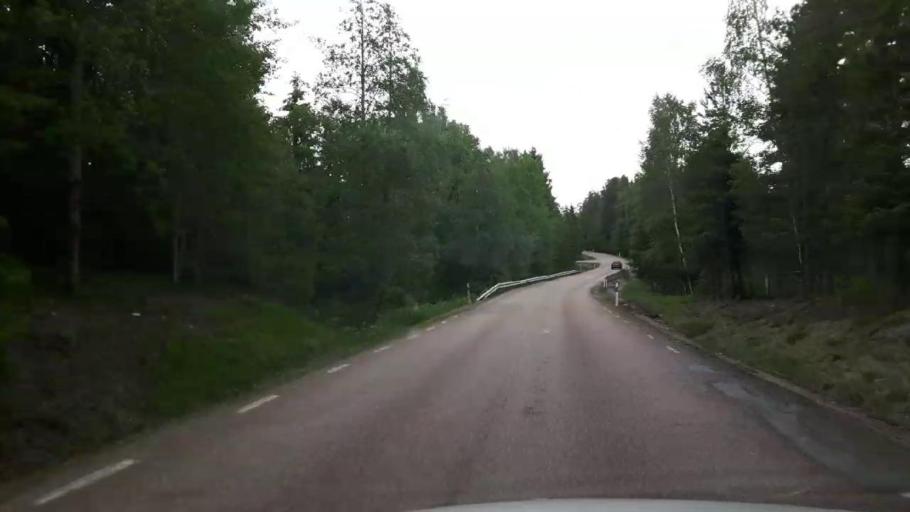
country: SE
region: Vaestmanland
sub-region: Skinnskattebergs Kommun
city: Skinnskatteberg
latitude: 59.8473
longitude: 15.8417
